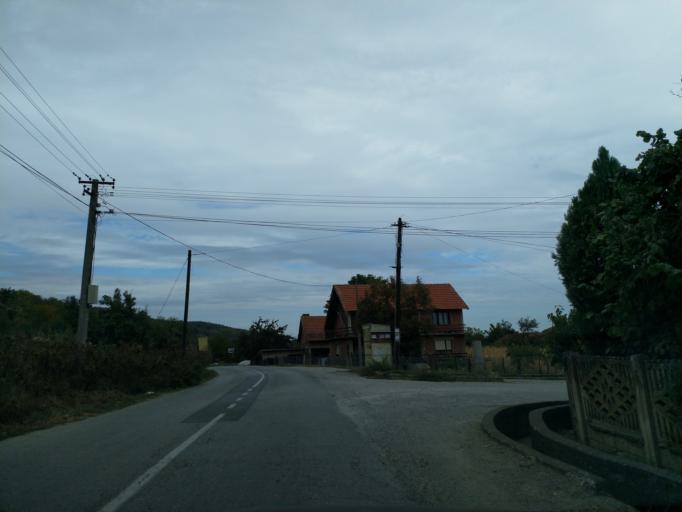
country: RS
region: Central Serbia
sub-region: Pomoravski Okrug
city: Paracin
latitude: 43.8428
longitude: 21.3227
